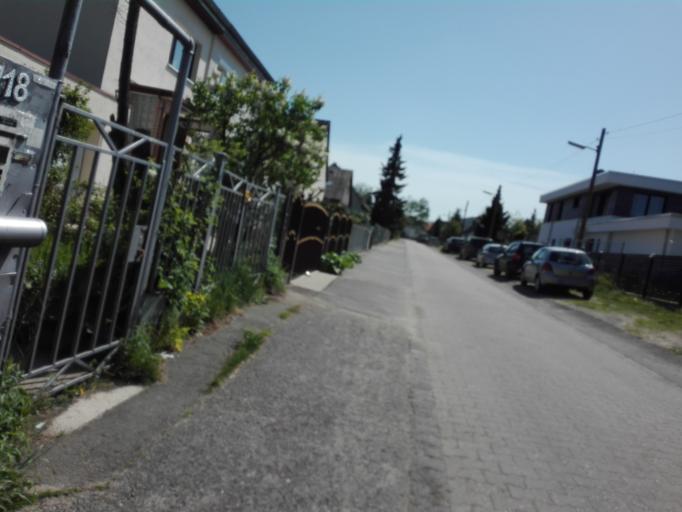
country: DE
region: Berlin
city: Rudow
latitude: 52.4061
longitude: 13.4840
